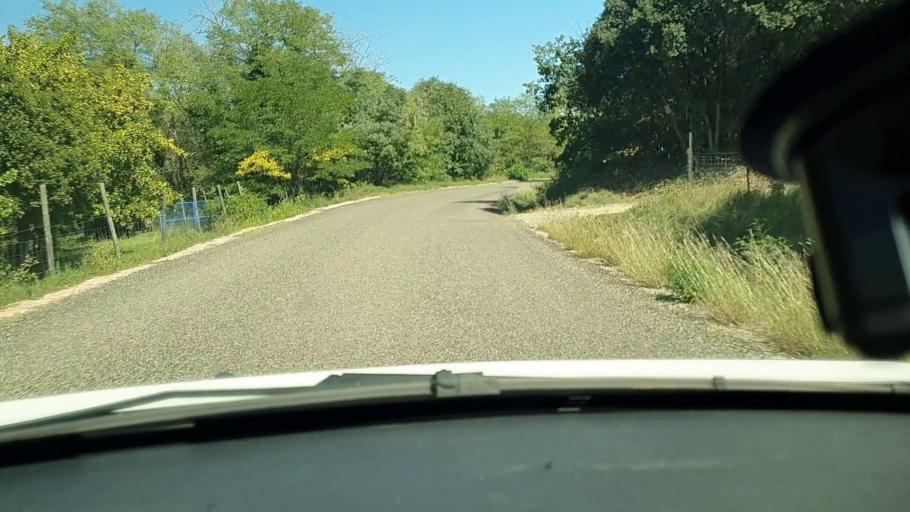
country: FR
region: Languedoc-Roussillon
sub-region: Departement du Gard
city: Goudargues
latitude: 44.1773
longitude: 4.4505
